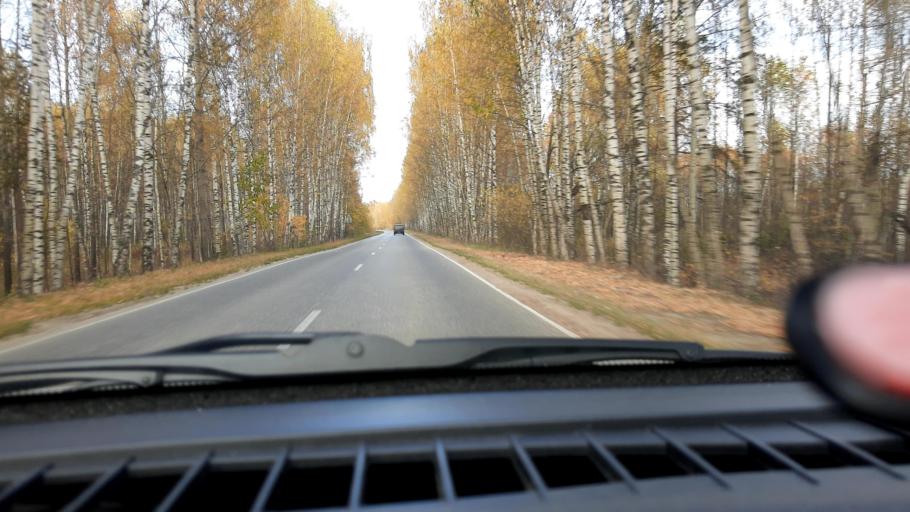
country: RU
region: Nizjnij Novgorod
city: Neklyudovo
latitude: 56.5181
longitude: 43.8373
